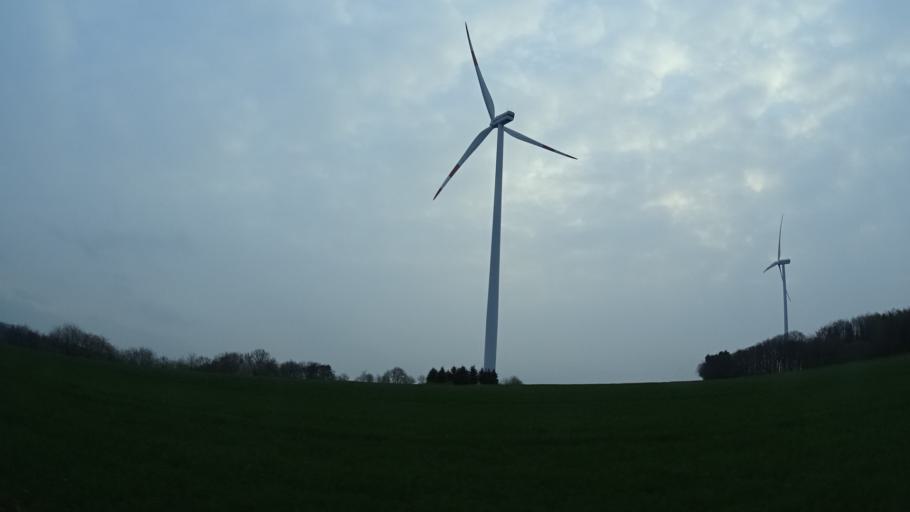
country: DE
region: Rheinland-Pfalz
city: Rimsberg
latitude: 49.6410
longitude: 7.2083
